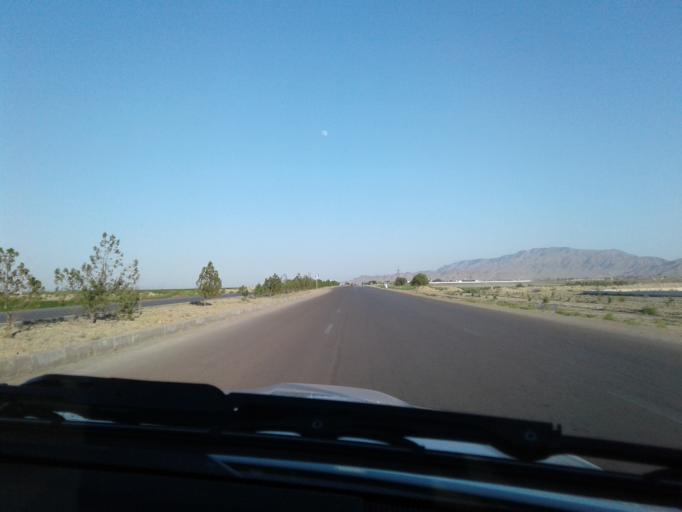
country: TM
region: Ahal
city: Baharly
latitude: 38.3322
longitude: 57.5775
